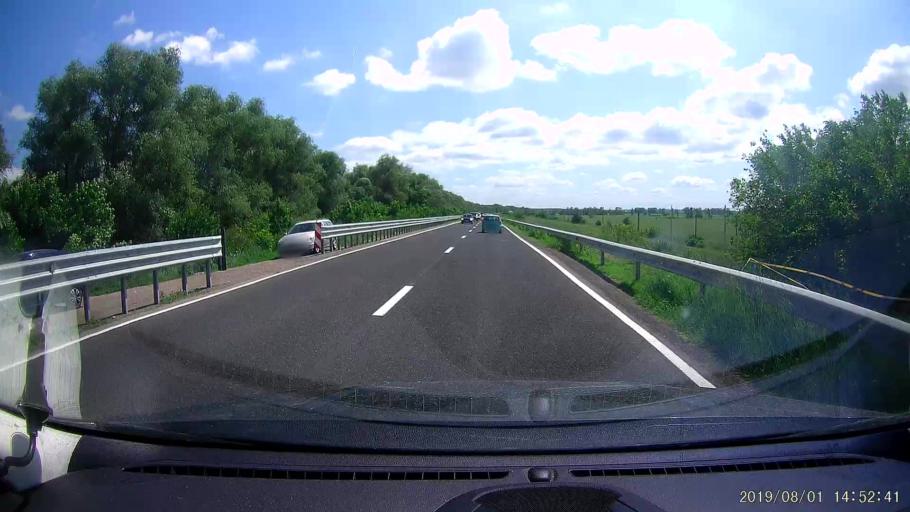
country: RO
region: Braila
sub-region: Comuna Vadeni
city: Vadeni
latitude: 45.3503
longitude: 28.0093
